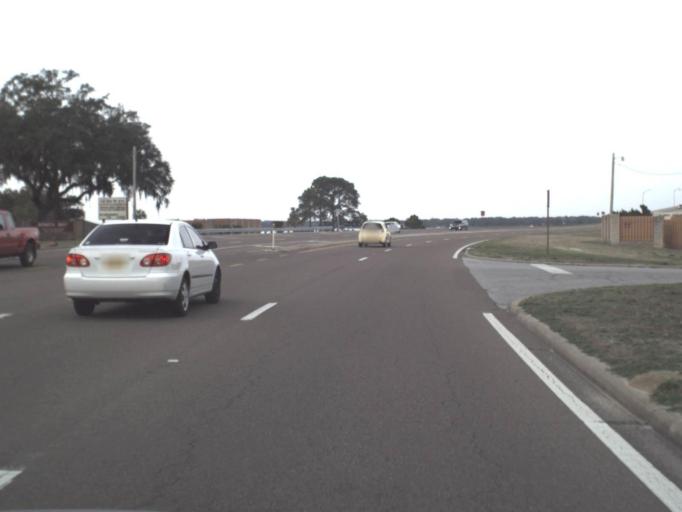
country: US
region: Florida
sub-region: Bay County
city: Tyndall Air Force Base
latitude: 30.0990
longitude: -85.6124
